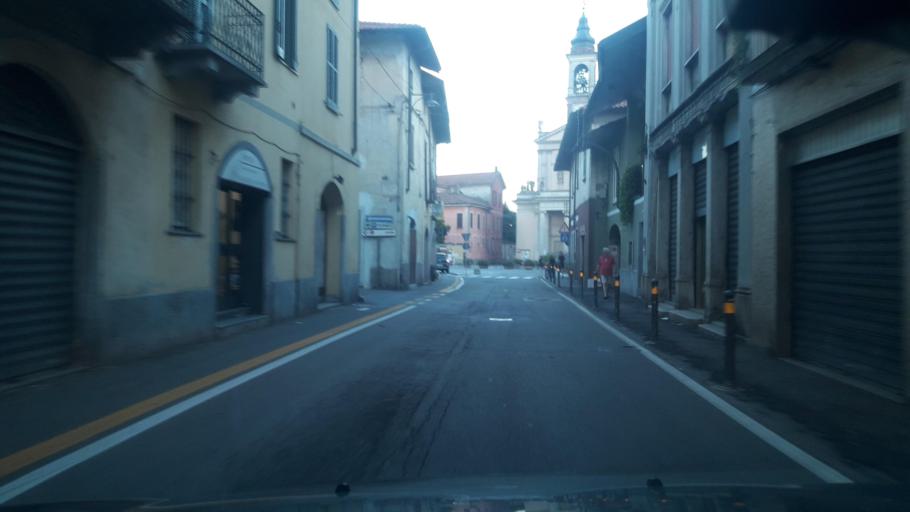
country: IT
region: Lombardy
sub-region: Citta metropolitana di Milano
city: Cuggiono
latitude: 45.5070
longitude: 8.8145
